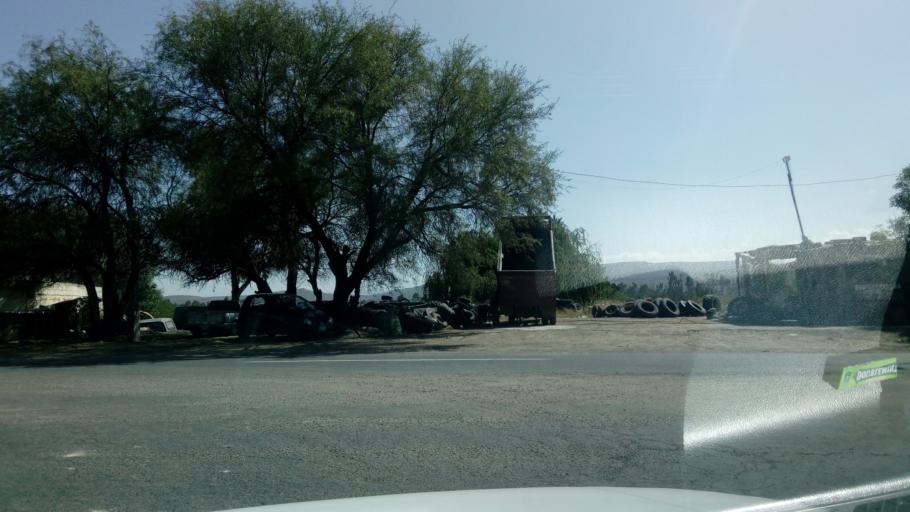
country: MX
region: Durango
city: Victoria de Durango
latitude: 23.9732
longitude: -104.6971
